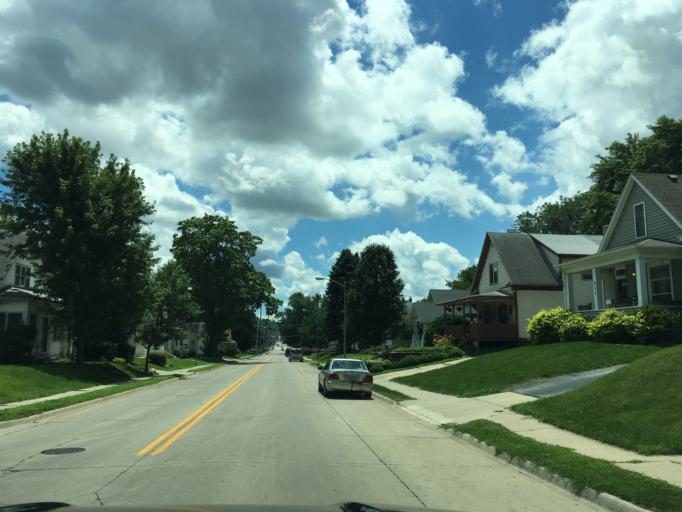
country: US
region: Nebraska
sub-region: Douglas County
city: Omaha
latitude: 41.2508
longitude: -95.9902
